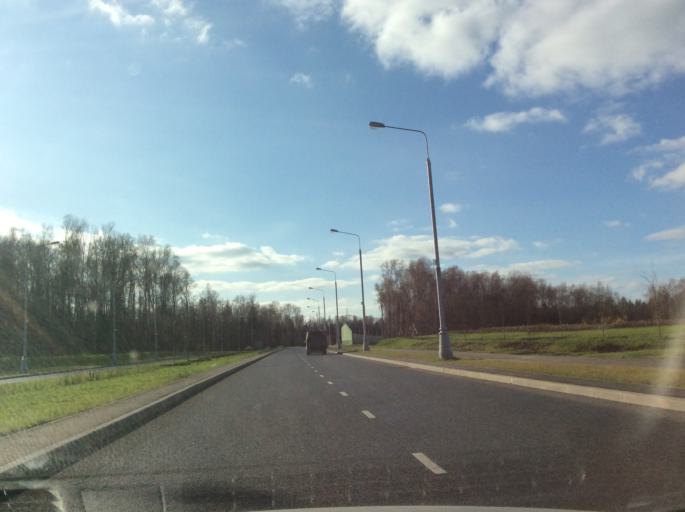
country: RU
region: Moskovskaya
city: Vatutinki
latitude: 55.4875
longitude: 37.3902
